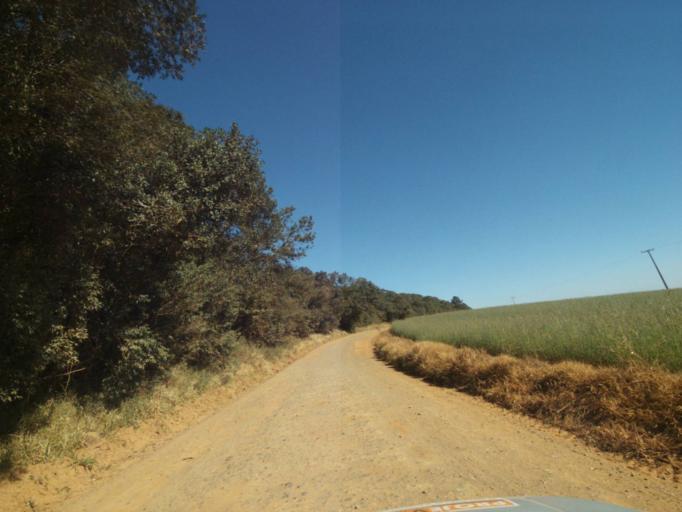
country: BR
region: Parana
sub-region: Tibagi
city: Tibagi
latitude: -24.6246
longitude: -50.6169
